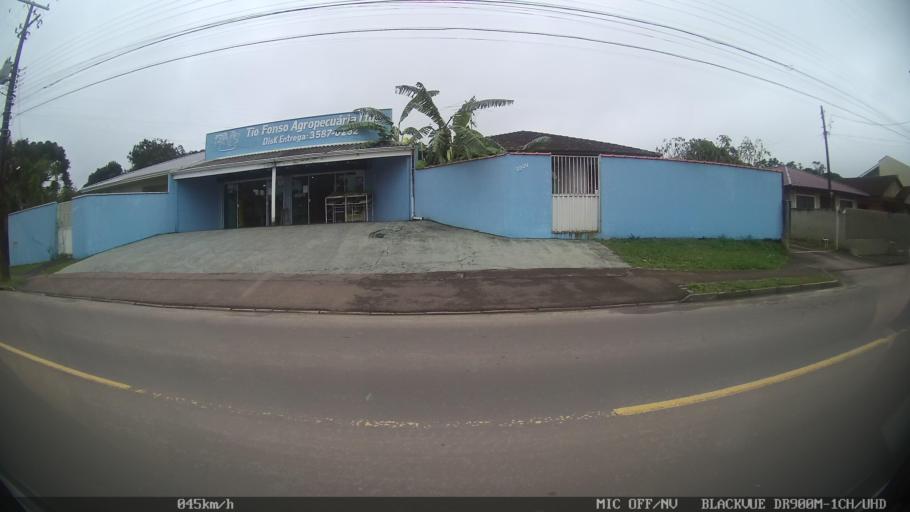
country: BR
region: Parana
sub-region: Sao Jose Dos Pinhais
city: Sao Jose dos Pinhais
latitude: -25.5833
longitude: -49.1709
